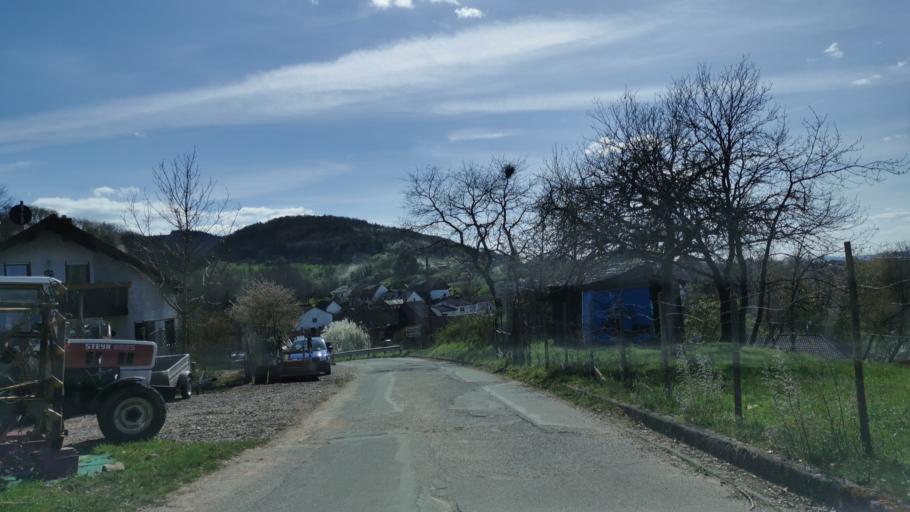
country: DE
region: Rheinland-Pfalz
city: Klausen
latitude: 49.9012
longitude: 6.8803
